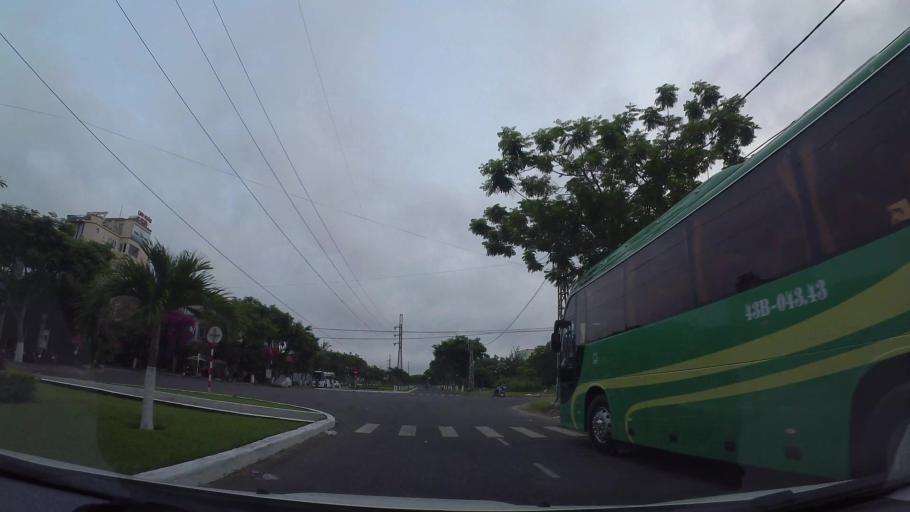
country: VN
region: Da Nang
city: Son Tra
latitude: 16.0470
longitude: 108.2362
